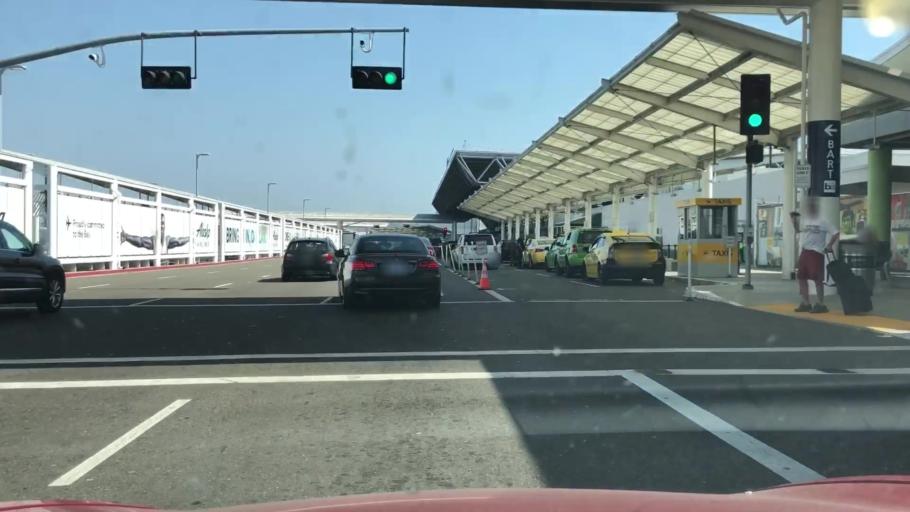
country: US
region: California
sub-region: Alameda County
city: San Leandro
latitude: 37.7126
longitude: -122.2132
